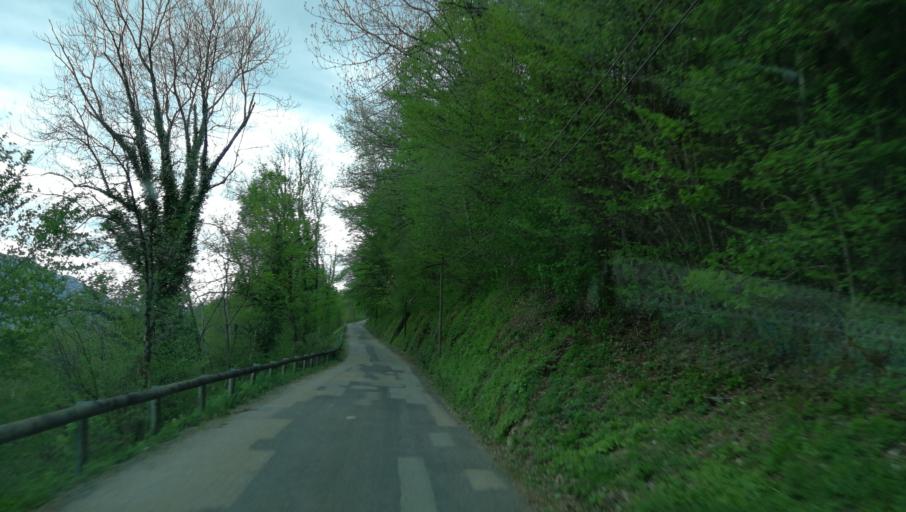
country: FR
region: Rhone-Alpes
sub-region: Departement de la Savoie
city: Brison-Saint-Innocent
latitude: 45.7142
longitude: 5.8529
